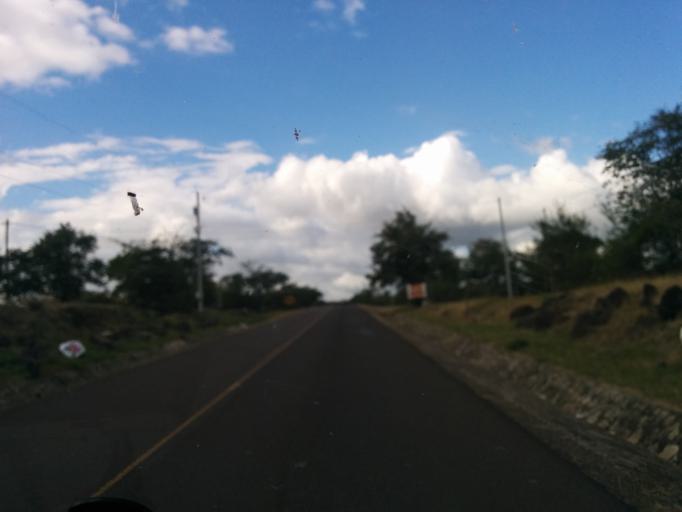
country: NI
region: Esteli
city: Esteli
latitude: 13.1960
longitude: -86.3736
